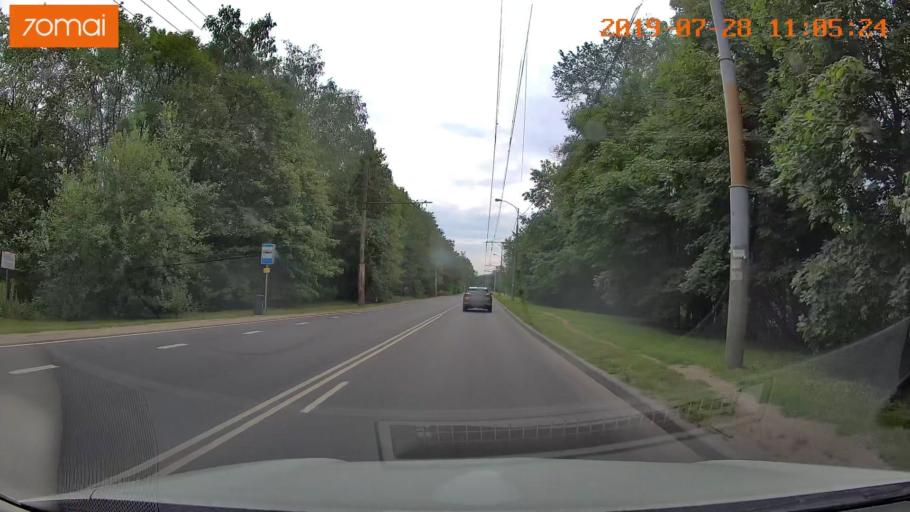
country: RU
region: Kaliningrad
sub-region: Gorod Kaliningrad
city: Kaliningrad
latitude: 54.7183
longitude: 20.3920
